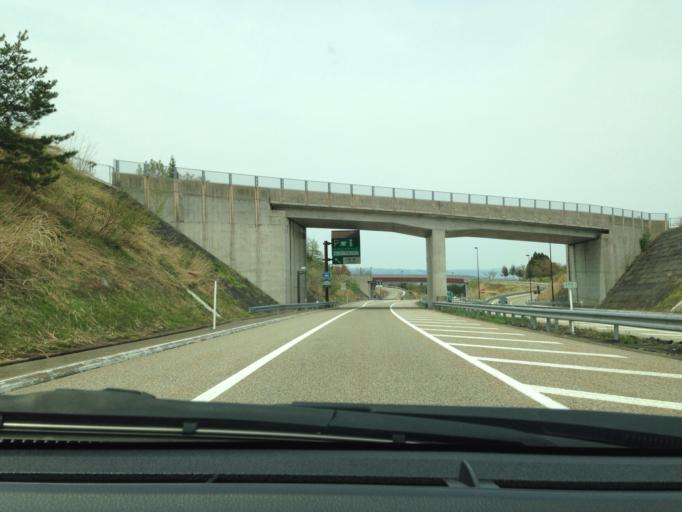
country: JP
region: Toyama
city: Fukumitsu
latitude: 36.5007
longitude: 136.8742
